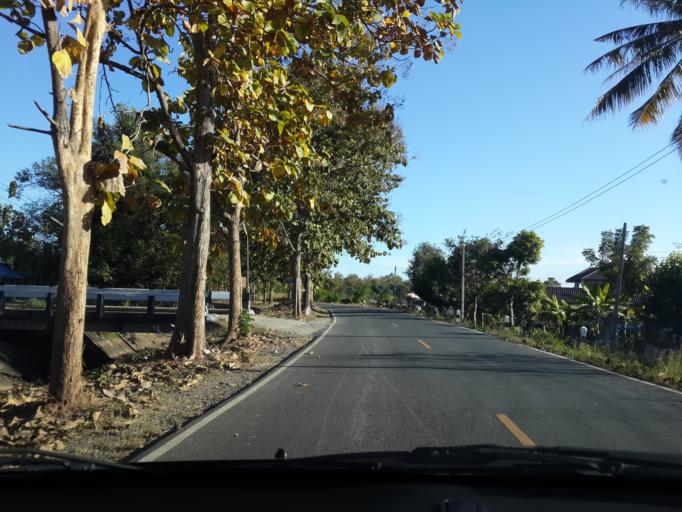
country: TH
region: Chiang Mai
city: San Sai
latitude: 18.8987
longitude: 99.1378
